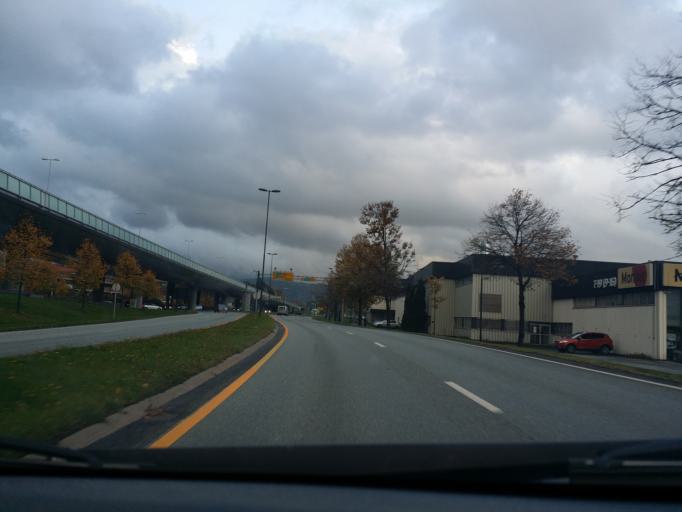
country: NO
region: Buskerud
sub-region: Drammen
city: Drammen
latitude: 59.7413
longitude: 10.2267
